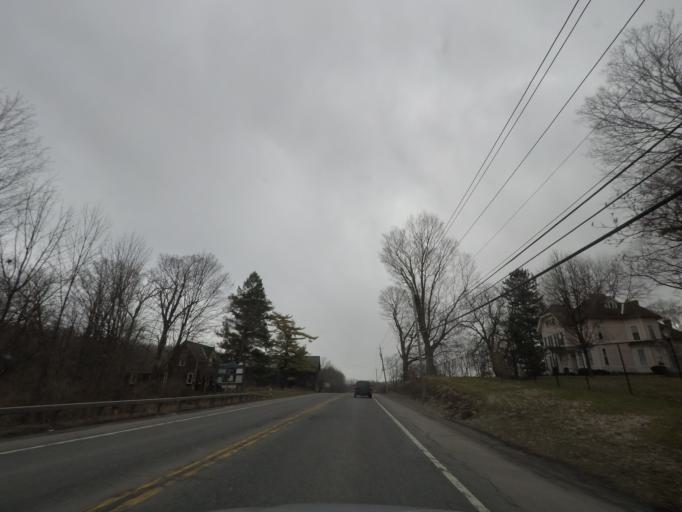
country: US
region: New York
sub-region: Onondaga County
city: Fayetteville
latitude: 43.0337
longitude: -75.9822
